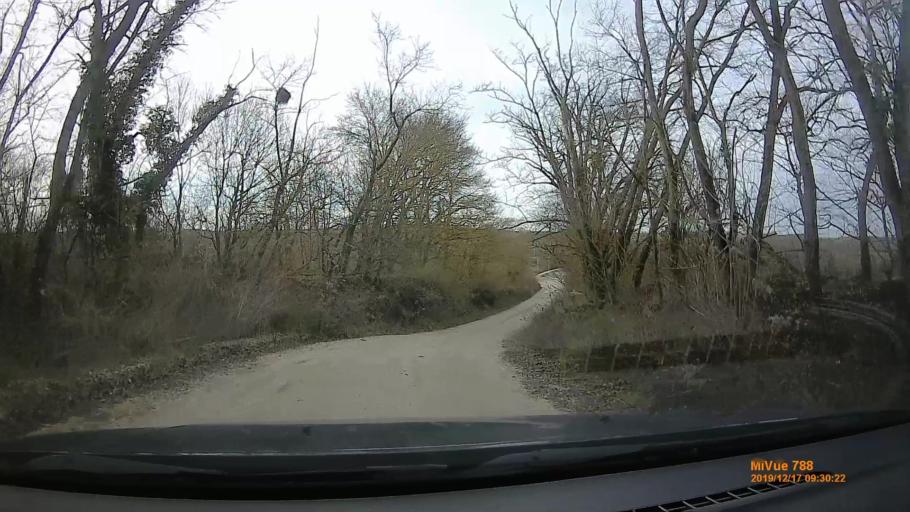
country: HU
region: Somogy
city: Karad
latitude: 46.6258
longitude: 17.8027
